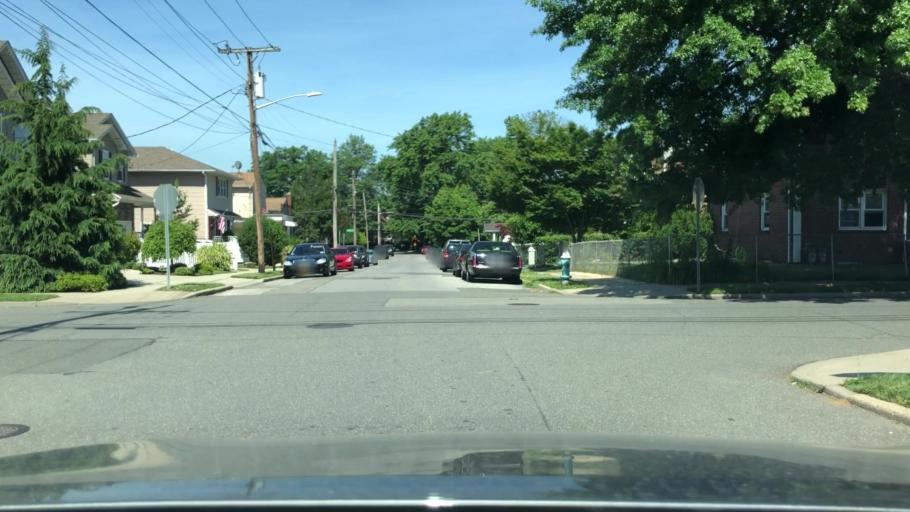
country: US
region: New York
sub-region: Nassau County
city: South Floral Park
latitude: 40.7016
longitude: -73.6969
